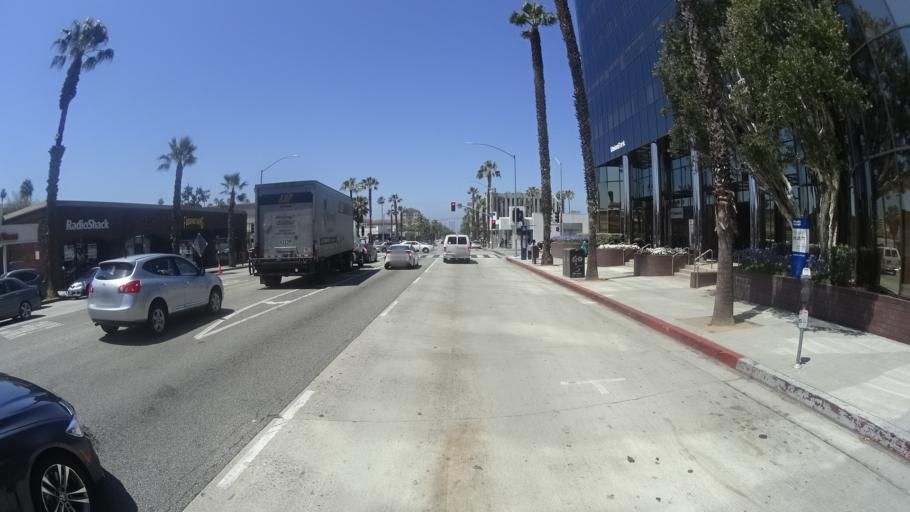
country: US
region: California
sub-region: Los Angeles County
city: Santa Monica
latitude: 34.0317
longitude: -118.4828
